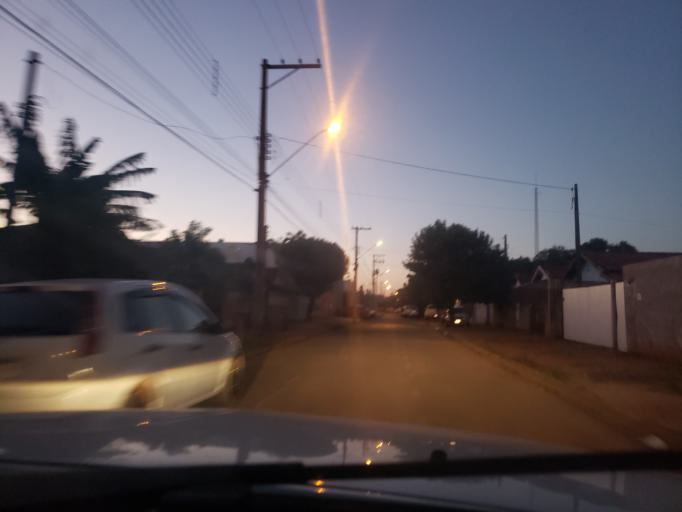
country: BR
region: Sao Paulo
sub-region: Conchal
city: Conchal
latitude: -22.2948
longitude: -47.1317
